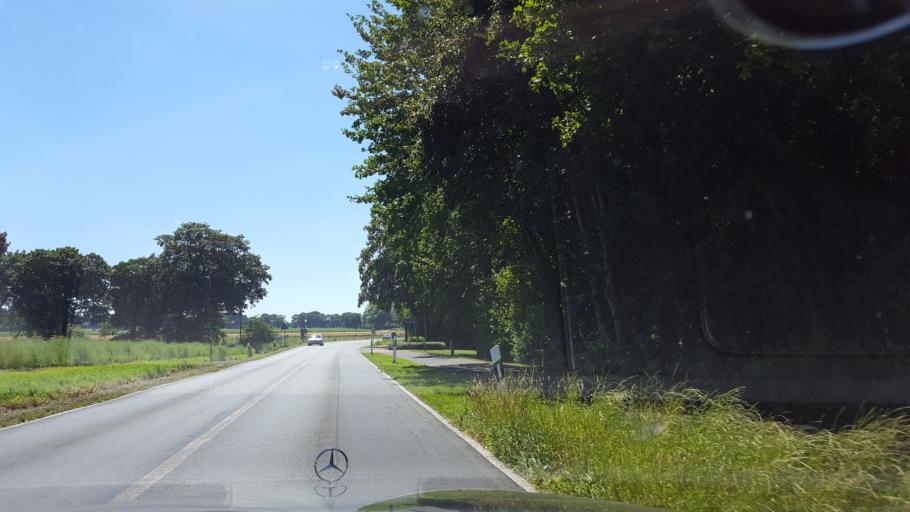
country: DE
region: North Rhine-Westphalia
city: Herten
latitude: 51.6399
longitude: 7.1555
